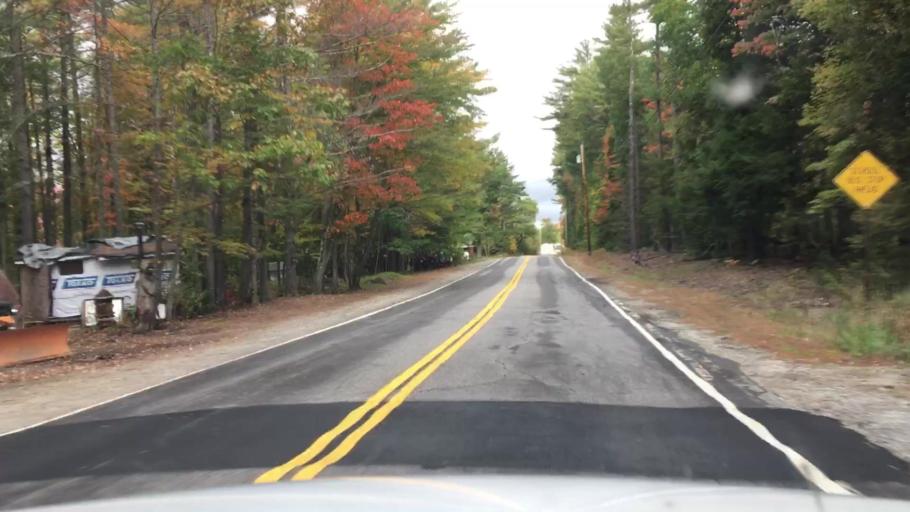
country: US
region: Maine
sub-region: Oxford County
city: Bethel
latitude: 44.3315
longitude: -70.7746
